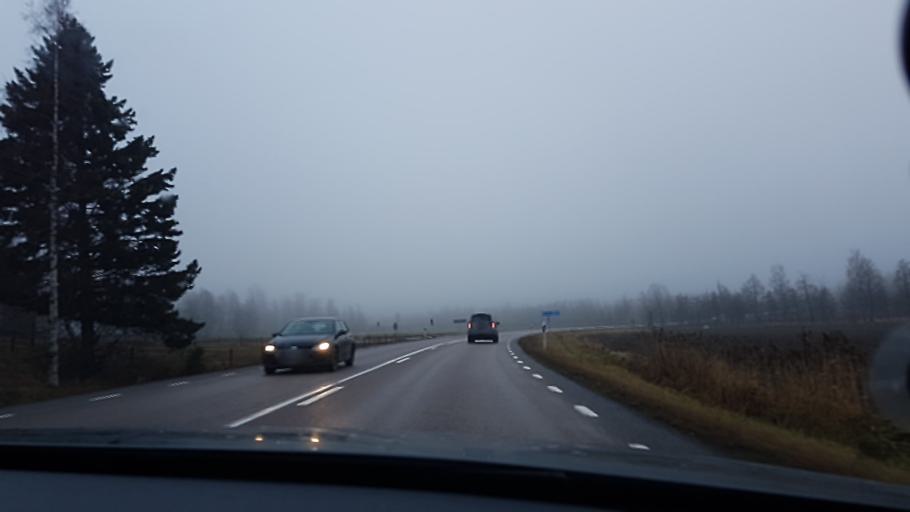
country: SE
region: Vaestra Goetaland
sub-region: Gullspangs Kommun
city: Gullspang
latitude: 58.9939
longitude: 14.1015
